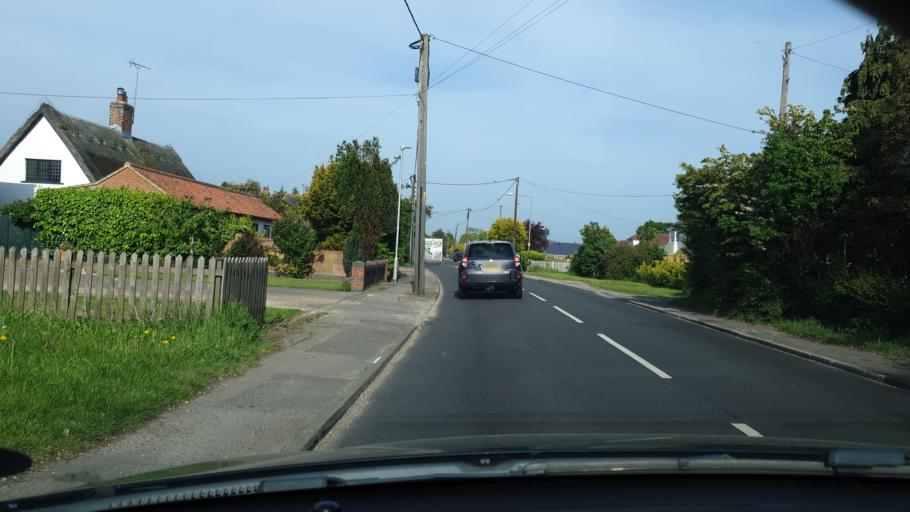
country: GB
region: England
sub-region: Essex
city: Frinton-on-Sea
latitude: 51.8443
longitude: 1.2079
